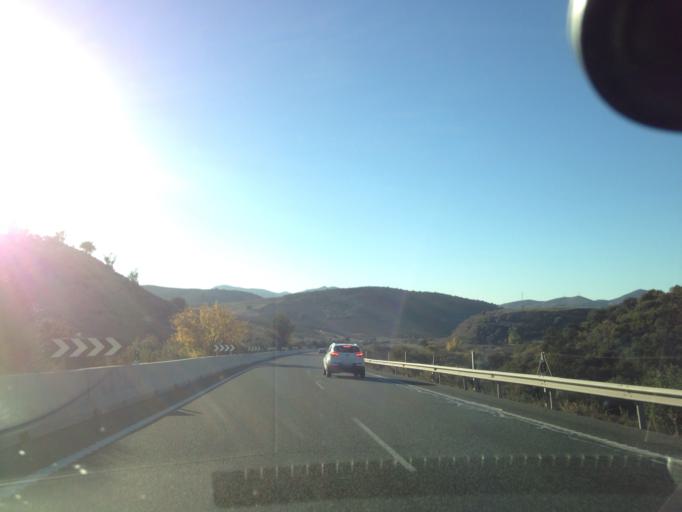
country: ES
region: Andalusia
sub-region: Provincia de Malaga
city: Casabermeja
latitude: 36.9458
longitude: -4.4412
